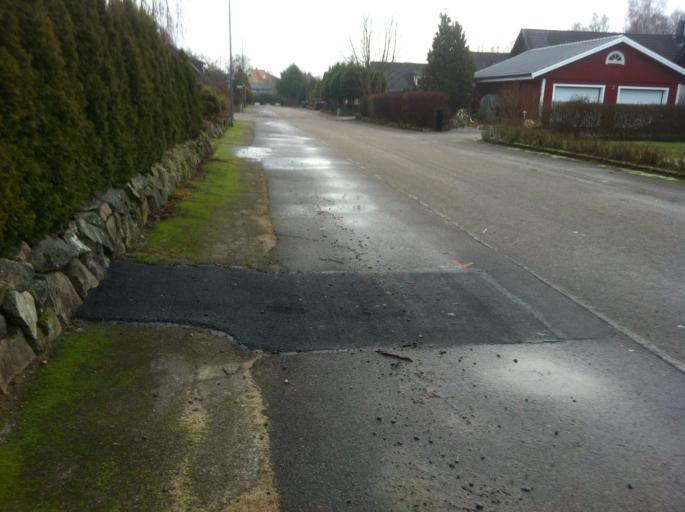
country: SE
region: Skane
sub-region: Perstorps Kommun
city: Perstorp
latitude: 56.1489
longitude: 13.3825
